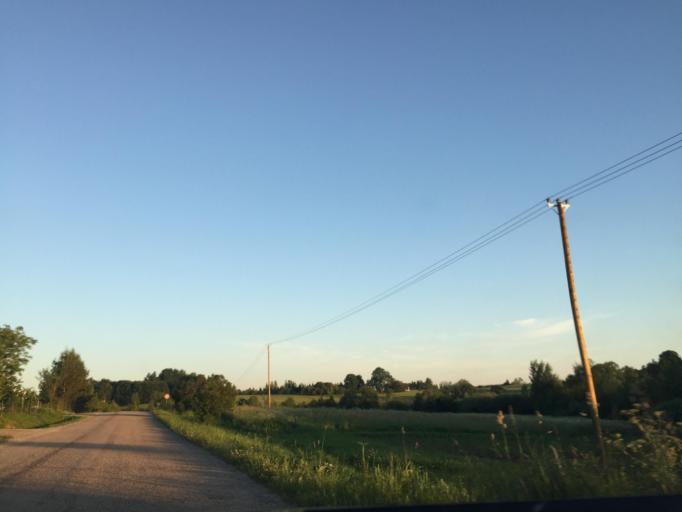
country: LV
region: Rezekne
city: Rezekne
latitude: 56.3682
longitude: 27.4089
